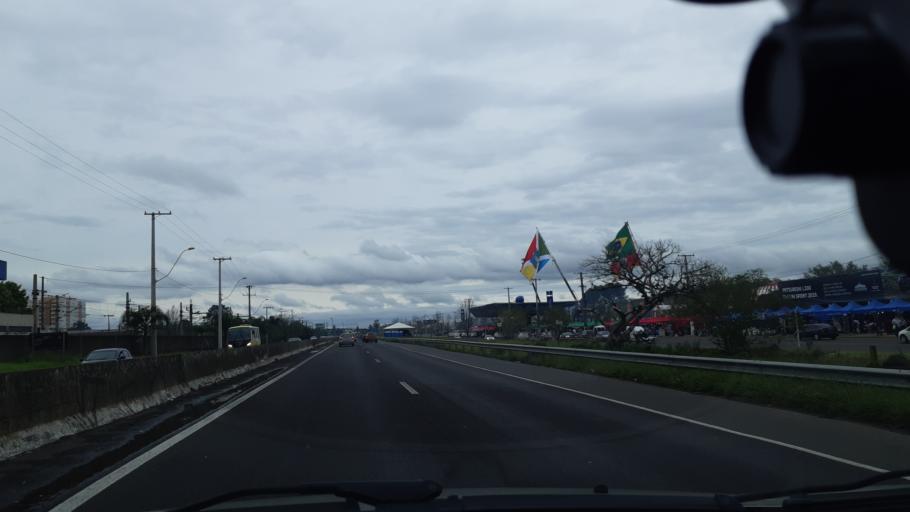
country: BR
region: Rio Grande do Sul
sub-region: Esteio
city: Esteio
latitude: -29.8520
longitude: -51.1797
